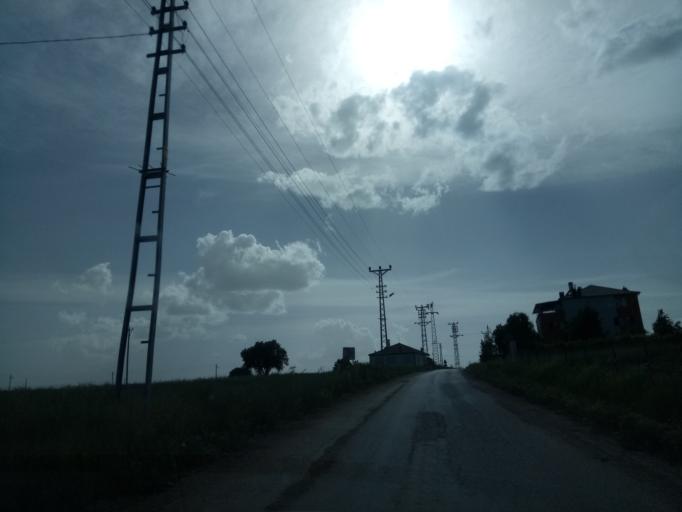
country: TR
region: Konya
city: Ahirli
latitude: 37.2842
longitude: 32.1797
